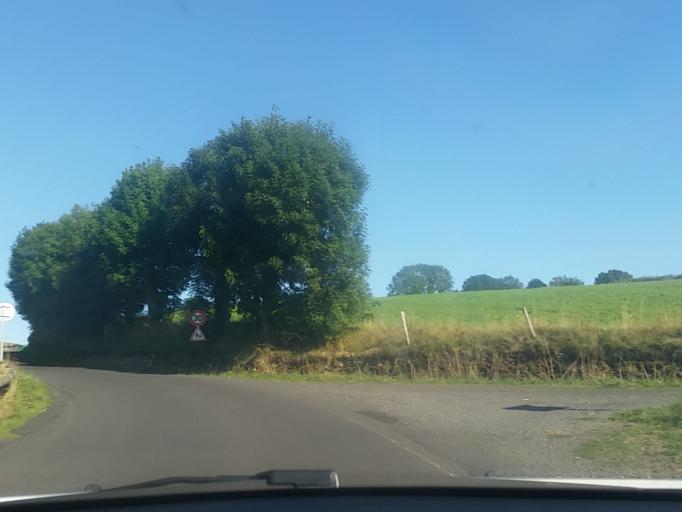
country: FR
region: Auvergne
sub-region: Departement du Cantal
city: Saint-Flour
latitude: 45.0248
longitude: 3.0647
